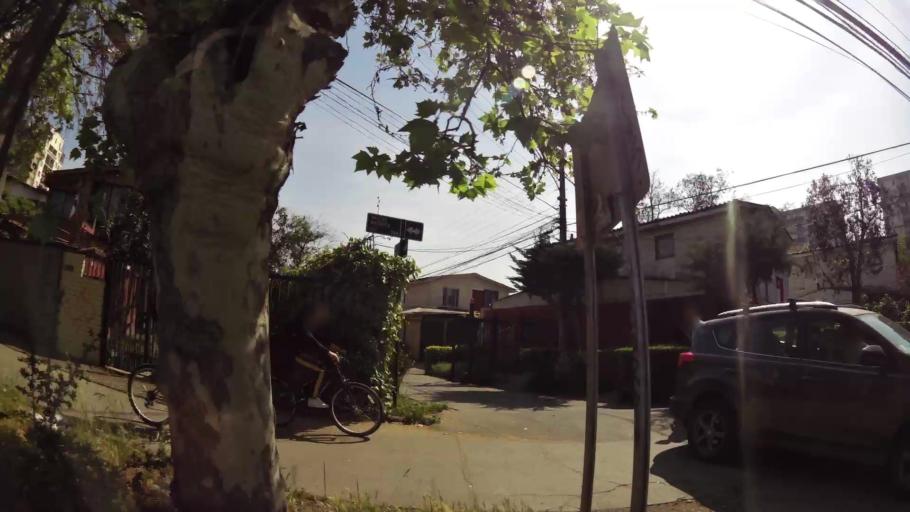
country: CL
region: Santiago Metropolitan
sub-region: Provincia de Santiago
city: Villa Presidente Frei, Nunoa, Santiago, Chile
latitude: -33.5226
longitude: -70.5884
